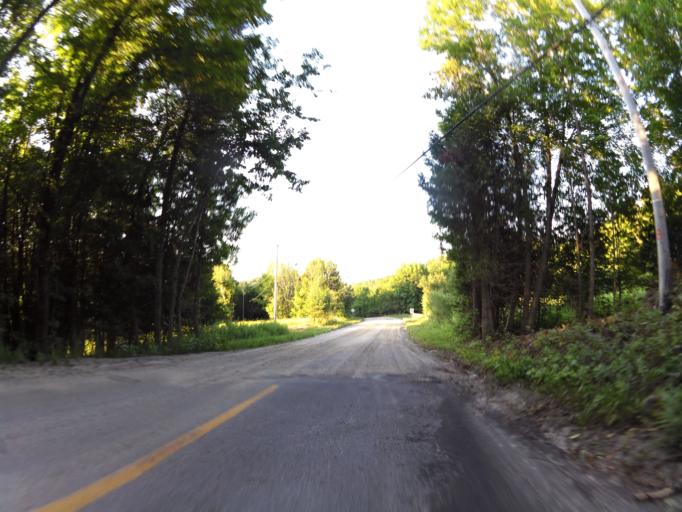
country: CA
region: Quebec
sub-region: Outaouais
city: Wakefield
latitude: 45.7390
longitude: -75.9732
